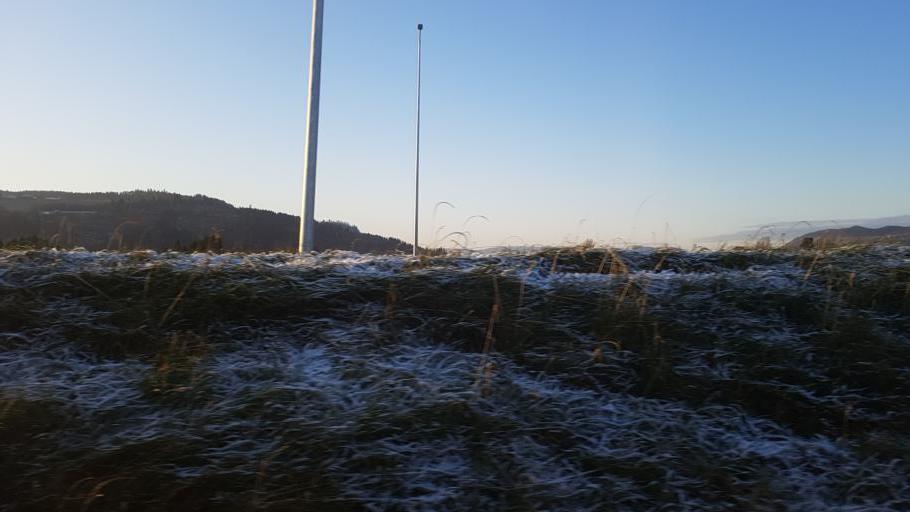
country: NO
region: Sor-Trondelag
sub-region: Melhus
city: Melhus
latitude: 63.3159
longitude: 10.2957
